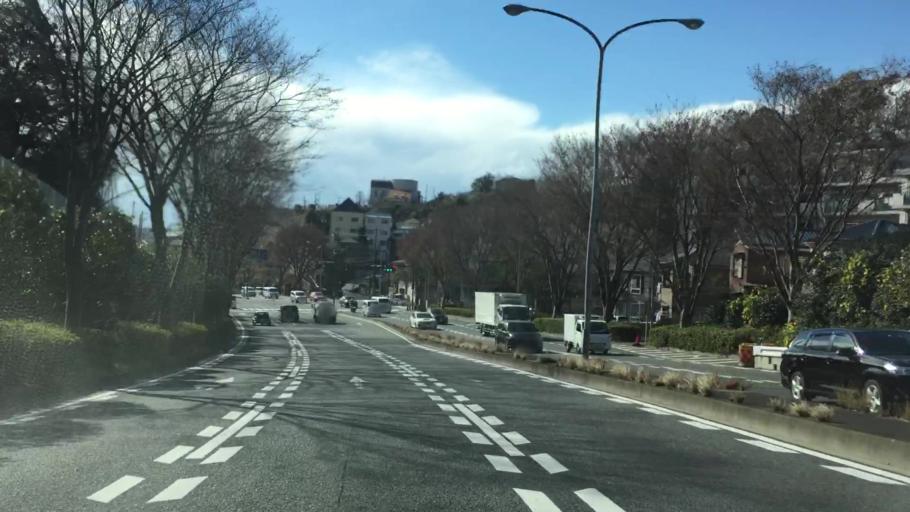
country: JP
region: Kanagawa
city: Yokohama
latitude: 35.4783
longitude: 139.5777
